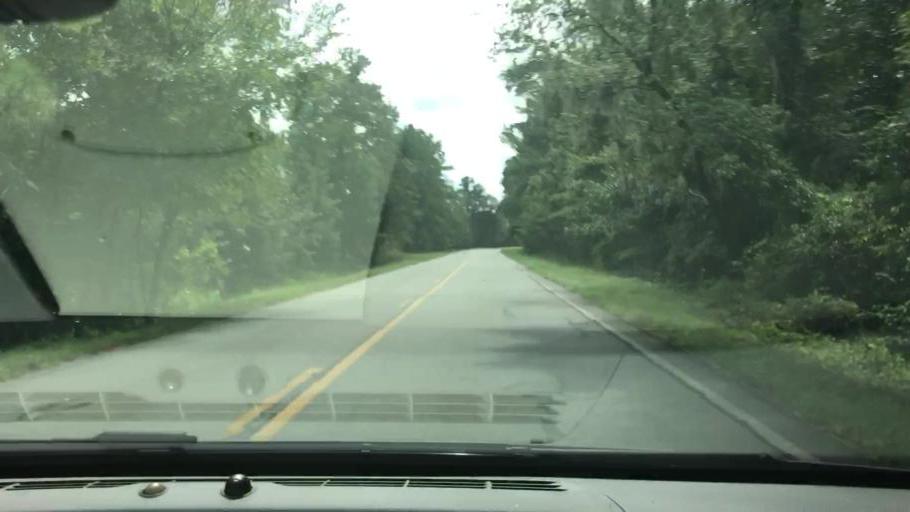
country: US
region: Georgia
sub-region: Quitman County
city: Georgetown
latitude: 32.0998
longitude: -85.0387
